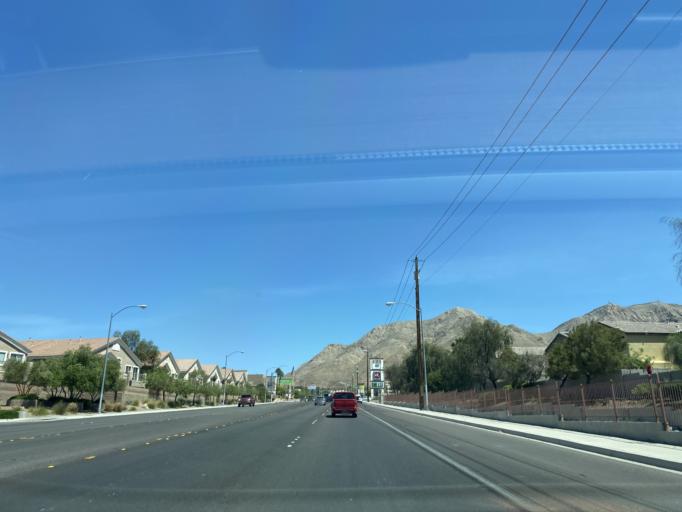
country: US
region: Nevada
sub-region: Clark County
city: Sunrise Manor
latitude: 36.1958
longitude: -115.0332
